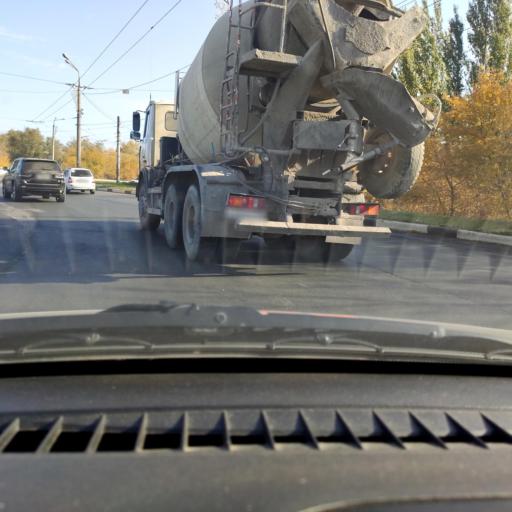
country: RU
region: Samara
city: Tol'yatti
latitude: 53.5529
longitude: 49.2879
